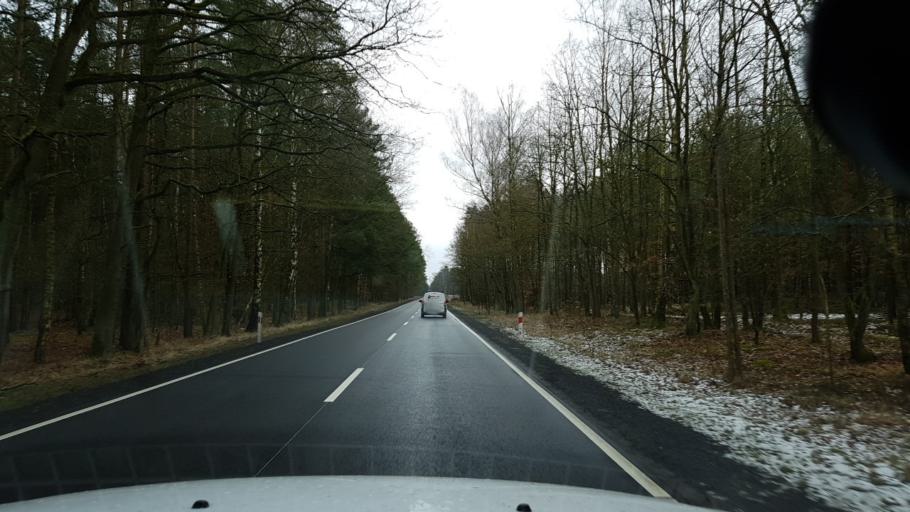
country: PL
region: West Pomeranian Voivodeship
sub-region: Powiat goleniowski
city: Stepnica
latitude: 53.6330
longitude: 14.6660
